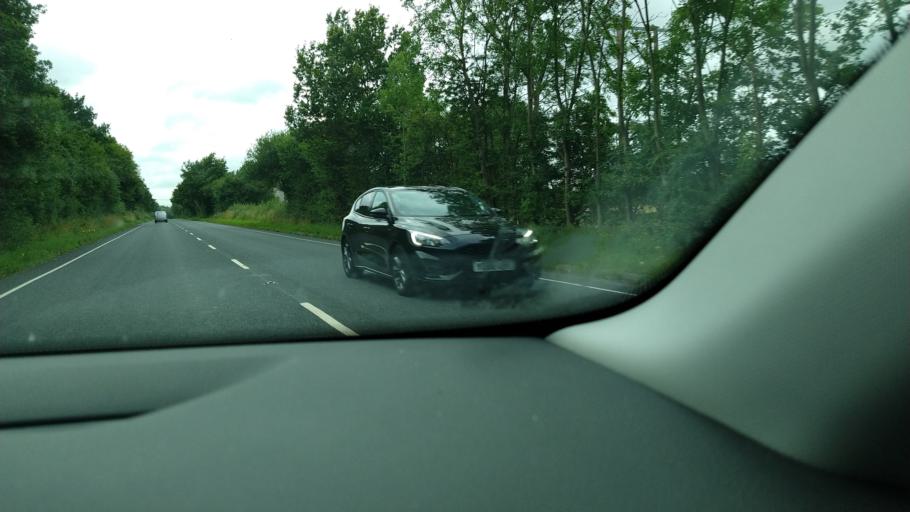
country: GB
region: England
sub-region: East Riding of Yorkshire
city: Barmby on the Marsh
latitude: 53.7202
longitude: -0.9748
